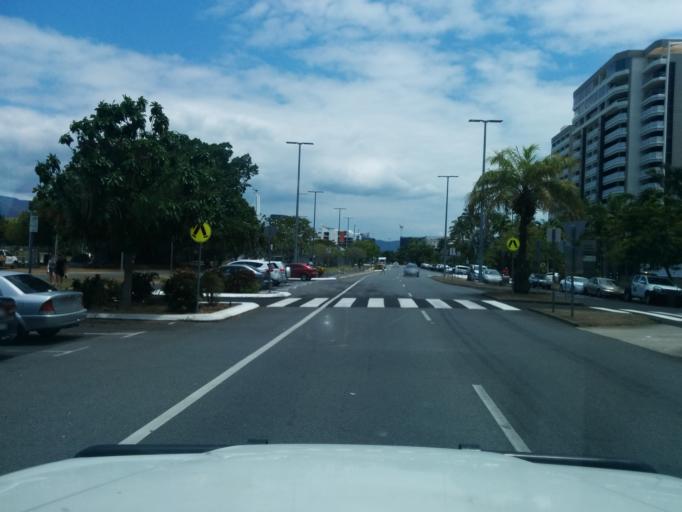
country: AU
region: Queensland
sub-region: Cairns
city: Cairns
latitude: -16.9125
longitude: 145.7693
